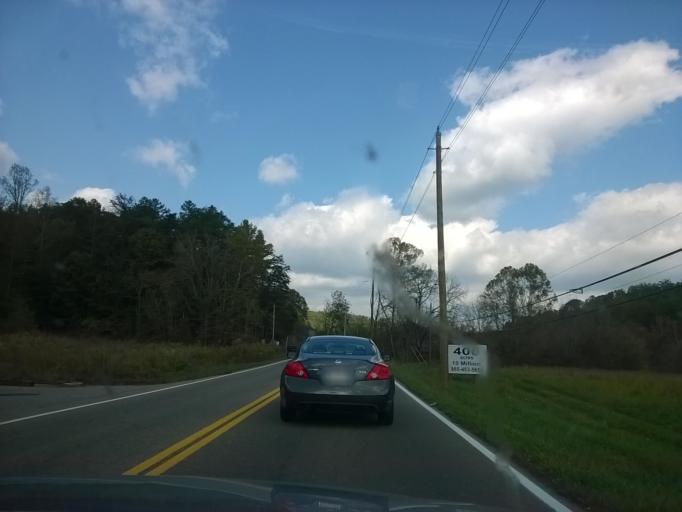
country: US
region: Tennessee
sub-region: Sevier County
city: Pigeon Forge
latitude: 35.7446
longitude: -83.6280
